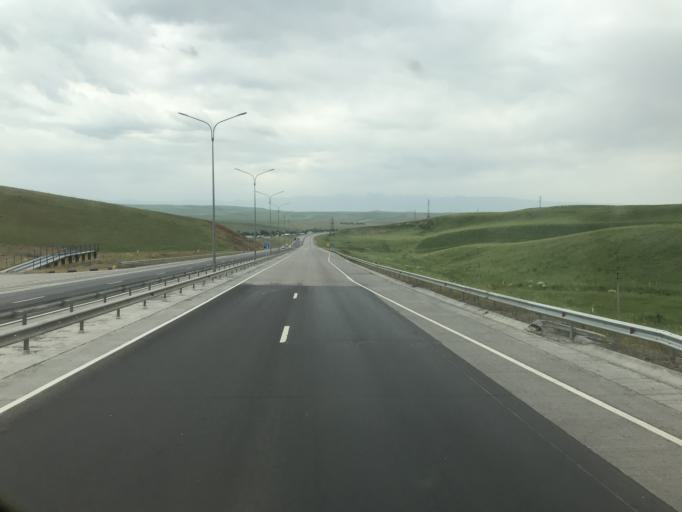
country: KZ
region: Ongtustik Qazaqstan
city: Qazyqurt
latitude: 41.9931
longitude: 69.4809
